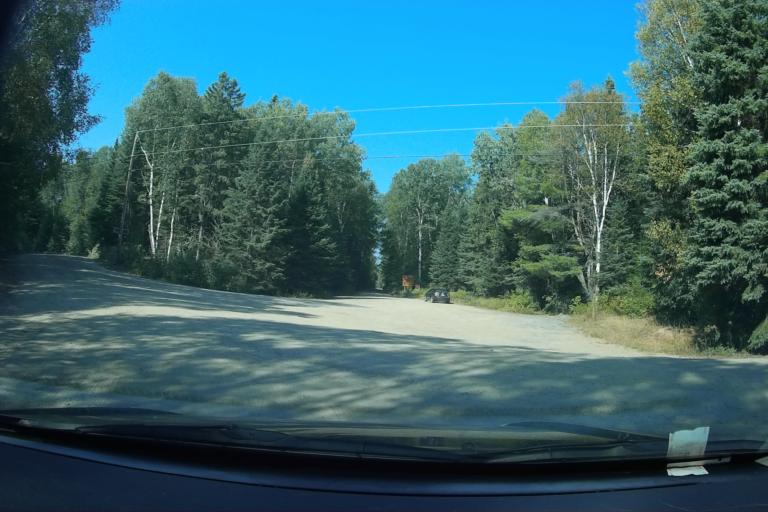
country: CA
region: Ontario
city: Huntsville
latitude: 45.5759
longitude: -78.7086
